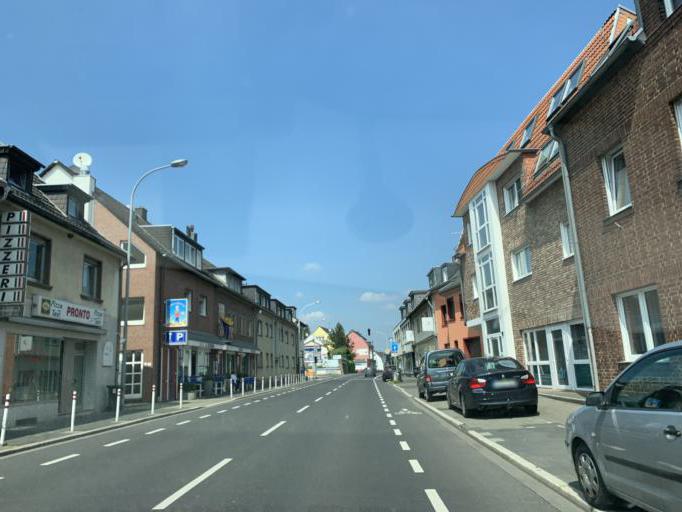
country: DE
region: North Rhine-Westphalia
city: Bruhl
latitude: 50.8147
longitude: 6.8891
